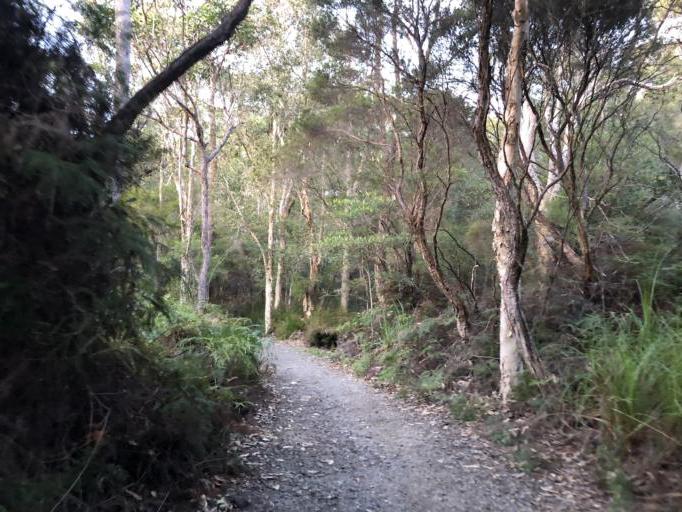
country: AU
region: New South Wales
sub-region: Coffs Harbour
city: Coffs Harbour
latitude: -30.3013
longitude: 153.1313
